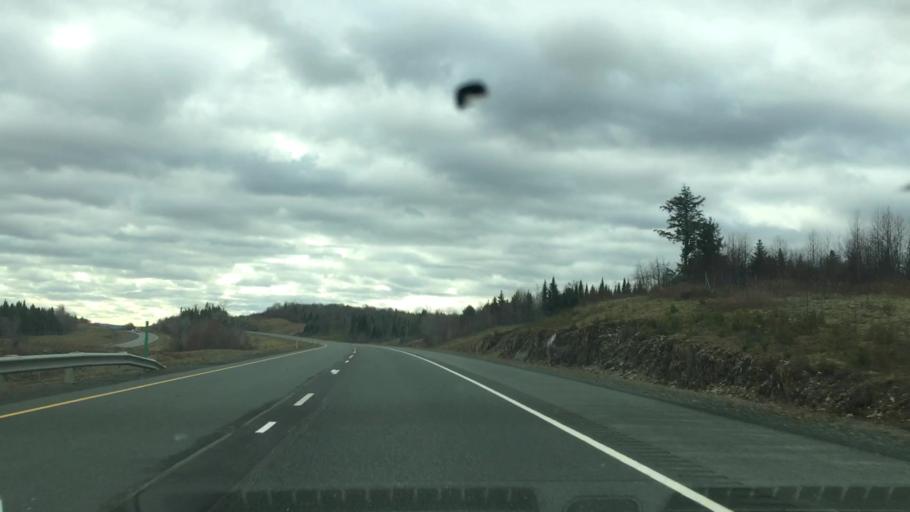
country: US
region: Maine
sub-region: Aroostook County
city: Fort Fairfield
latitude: 46.6423
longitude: -67.7444
